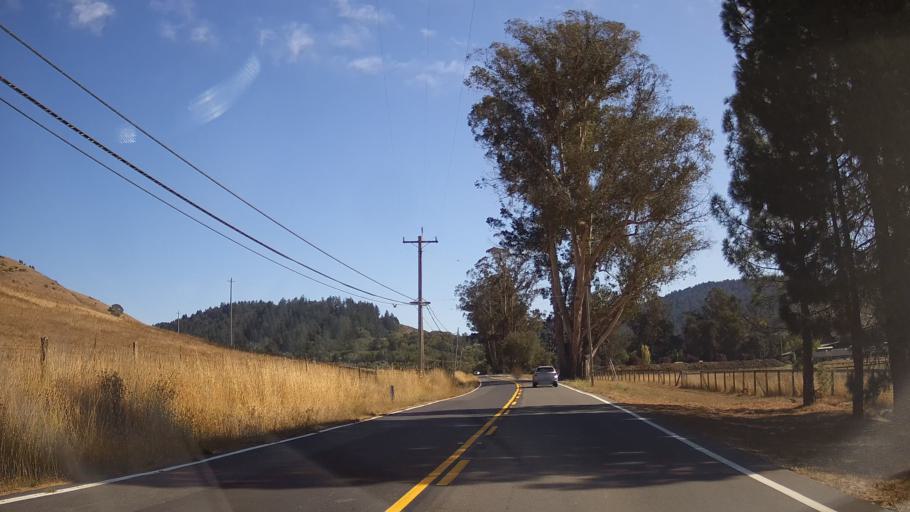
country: US
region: California
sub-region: Marin County
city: Lagunitas-Forest Knolls
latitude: 38.0587
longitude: -122.6964
